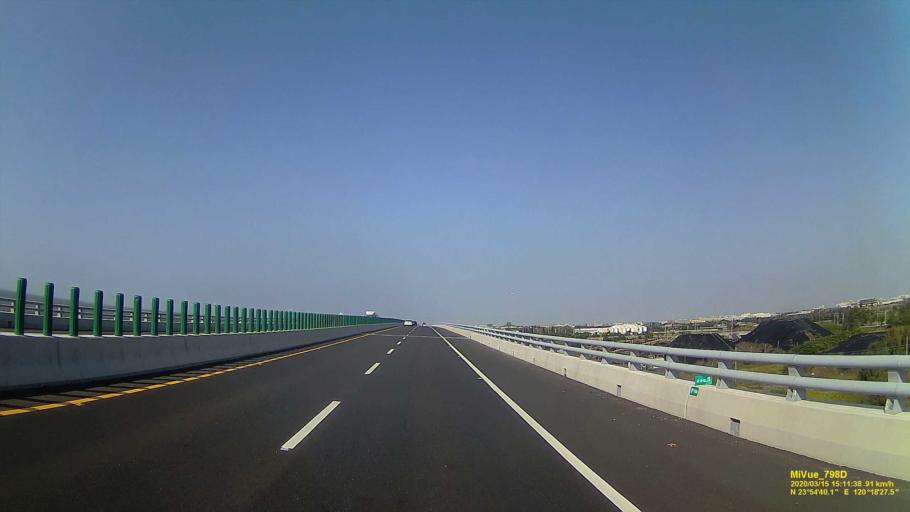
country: TW
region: Taiwan
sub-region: Changhua
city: Chang-hua
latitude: 23.9113
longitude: 120.3076
